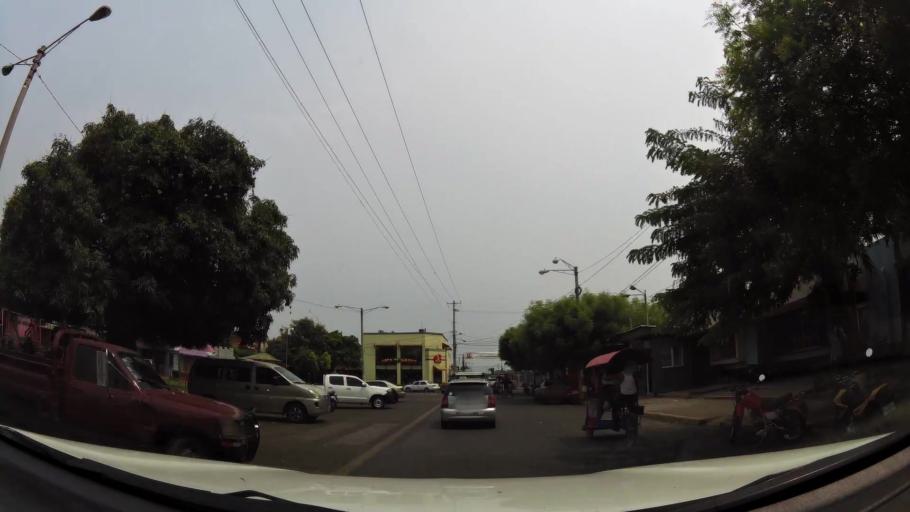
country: NI
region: Chinandega
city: Chinandega
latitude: 12.6313
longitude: -87.1352
